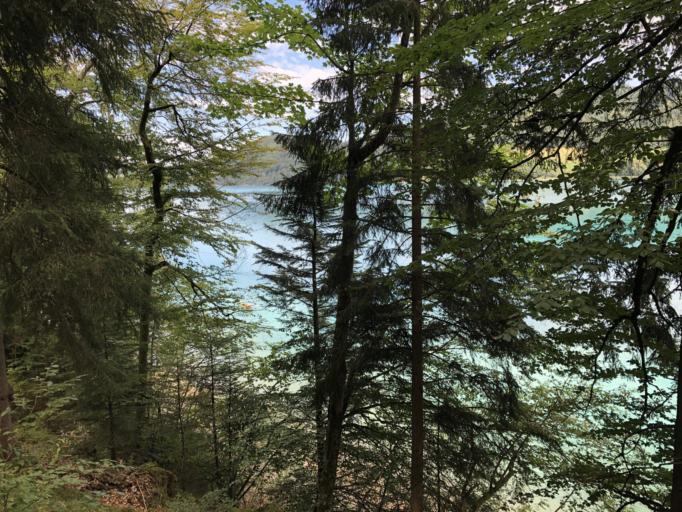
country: AT
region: Salzburg
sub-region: Politischer Bezirk Salzburg-Umgebung
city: Fuschl am See
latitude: 47.8001
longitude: 13.2745
